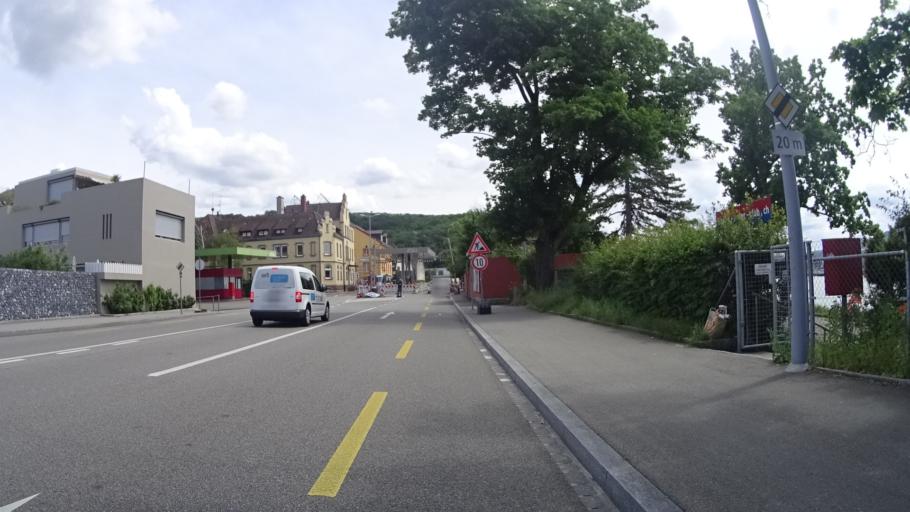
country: CH
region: Basel-Landschaft
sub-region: Bezirk Arlesheim
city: Birsfelden
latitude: 47.5624
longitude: 7.6340
